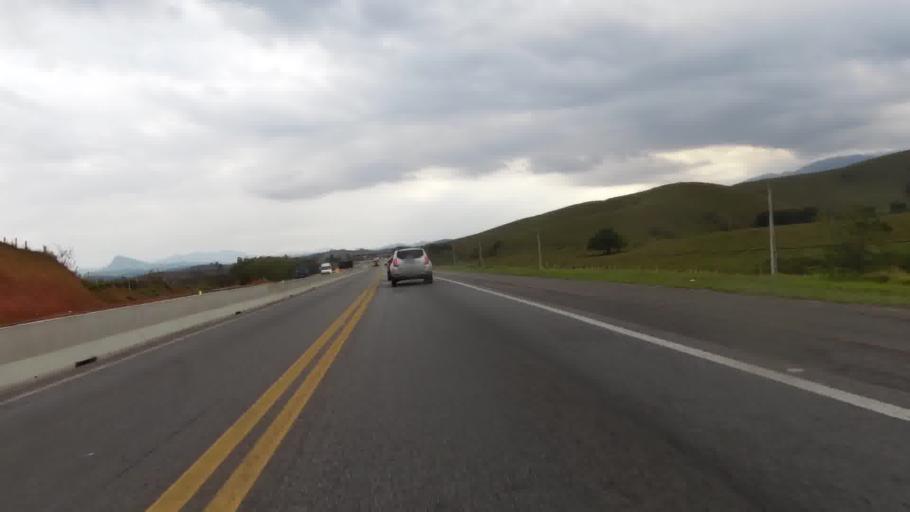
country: BR
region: Rio de Janeiro
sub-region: Rio Bonito
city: Rio Bonito
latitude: -22.6830
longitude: -42.5353
